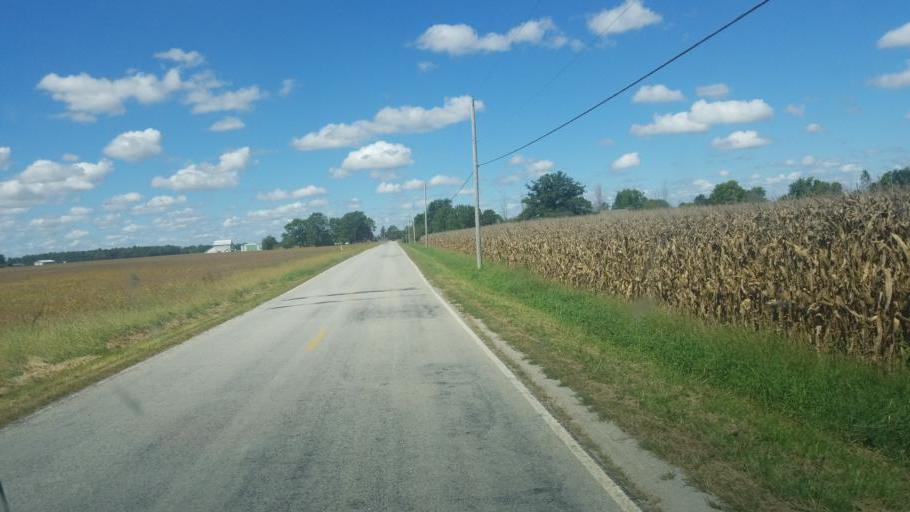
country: US
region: Ohio
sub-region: Madison County
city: West Jefferson
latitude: 39.9912
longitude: -83.2865
